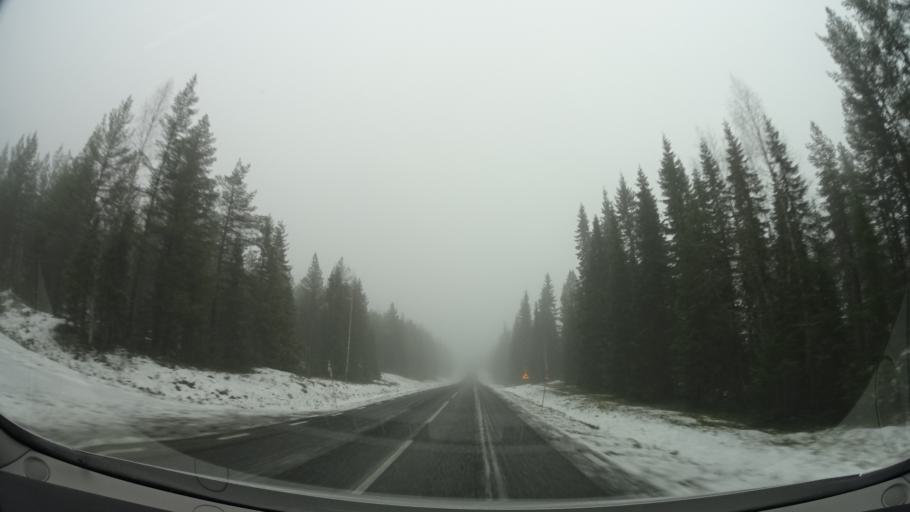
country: SE
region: Vaesterbotten
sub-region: Asele Kommun
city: Insjon
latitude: 64.3492
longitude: 17.8490
